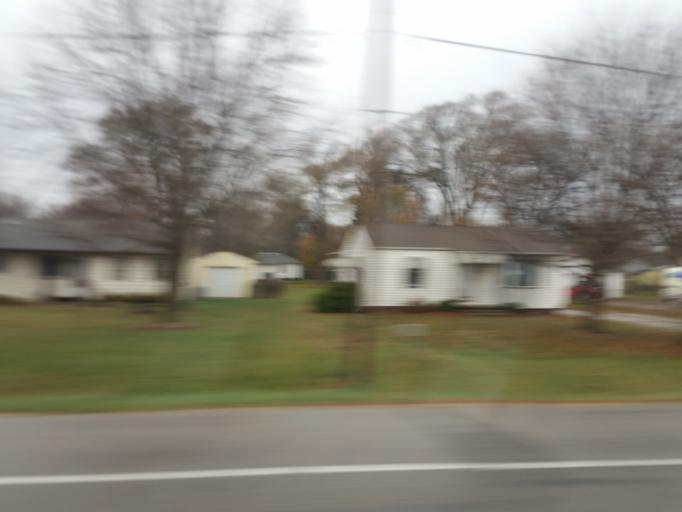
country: US
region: Iowa
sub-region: Black Hawk County
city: Elk Run Heights
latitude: 42.4102
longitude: -92.2658
